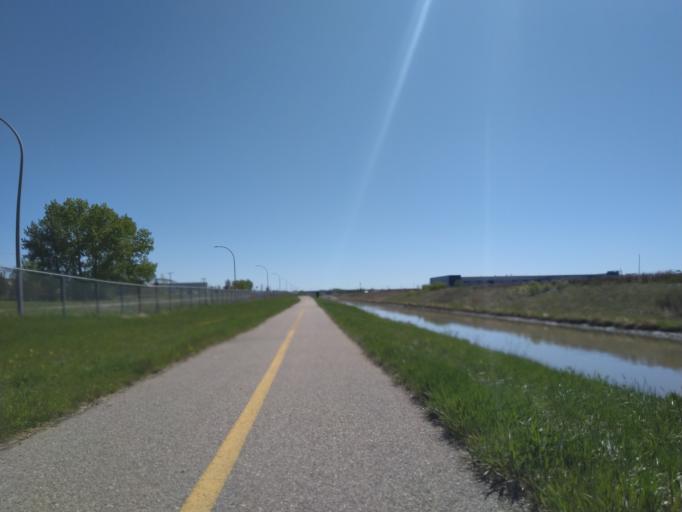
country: CA
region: Alberta
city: Calgary
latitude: 50.9657
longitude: -113.9775
